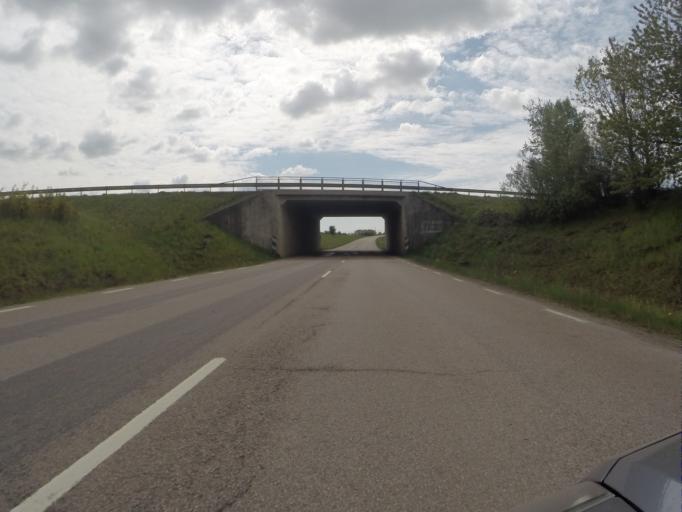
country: SE
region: Skane
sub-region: Helsingborg
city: Hyllinge
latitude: 56.0900
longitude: 12.8044
